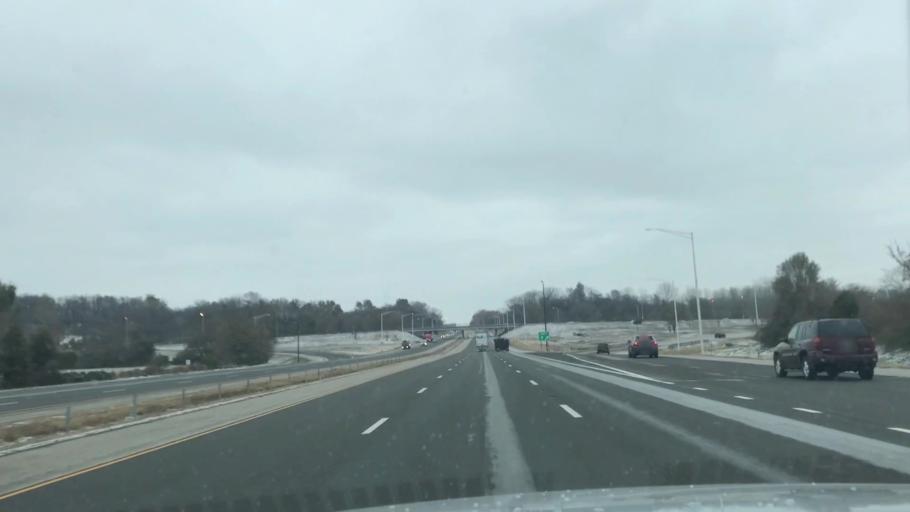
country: US
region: Illinois
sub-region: Madison County
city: Glen Carbon
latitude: 38.7565
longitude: -90.0137
